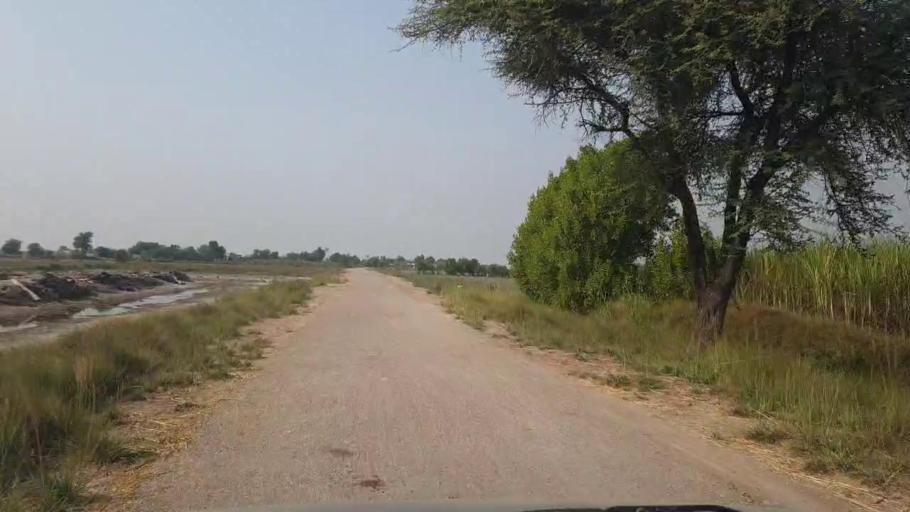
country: PK
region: Sindh
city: Tando Muhammad Khan
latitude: 25.0504
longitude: 68.3700
